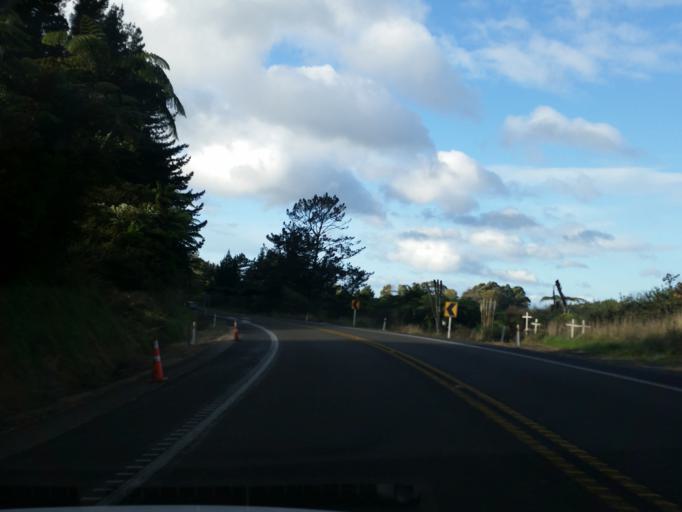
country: NZ
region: Bay of Plenty
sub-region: Western Bay of Plenty District
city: Katikati
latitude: -37.6480
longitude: 175.9820
